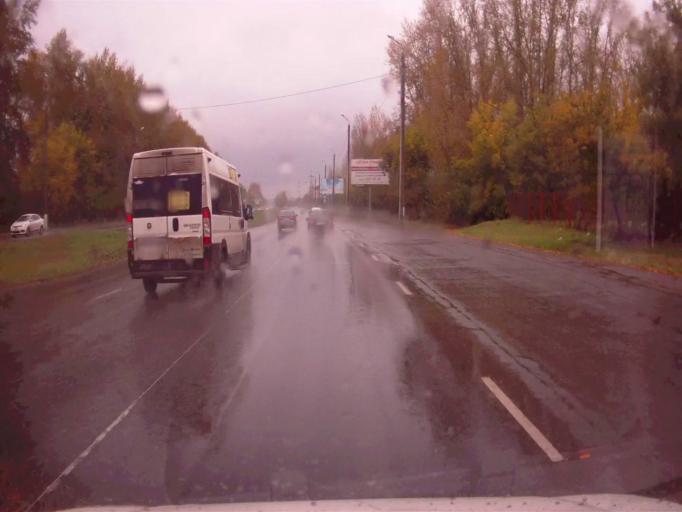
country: RU
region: Chelyabinsk
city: Dolgoderevenskoye
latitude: 55.2432
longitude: 61.3605
